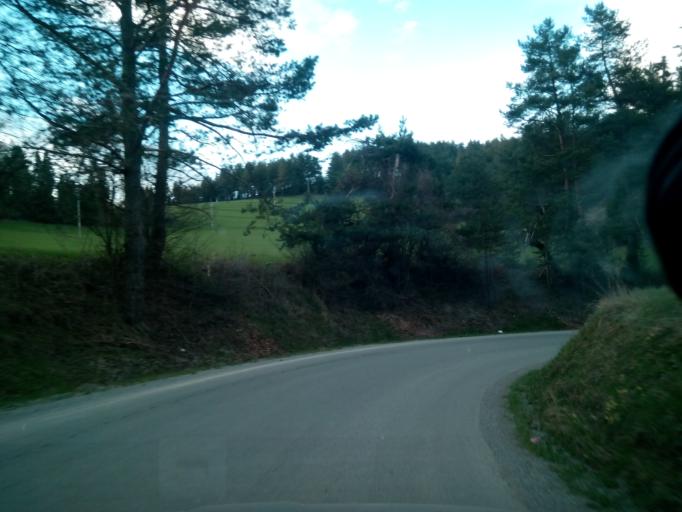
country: PL
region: Lesser Poland Voivodeship
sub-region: Powiat nowotarski
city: Niedzica
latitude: 49.3355
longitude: 20.3139
